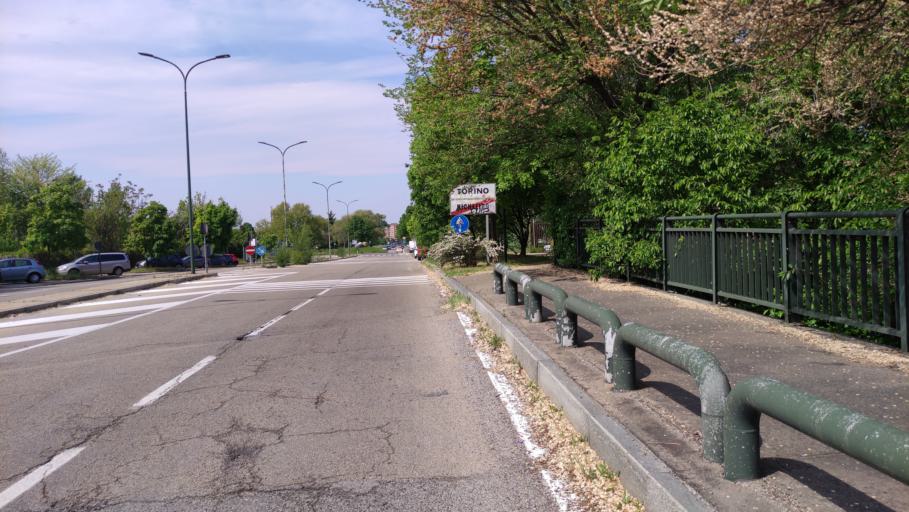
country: IT
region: Piedmont
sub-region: Provincia di Torino
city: Nichelino
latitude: 45.0080
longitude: 7.6502
